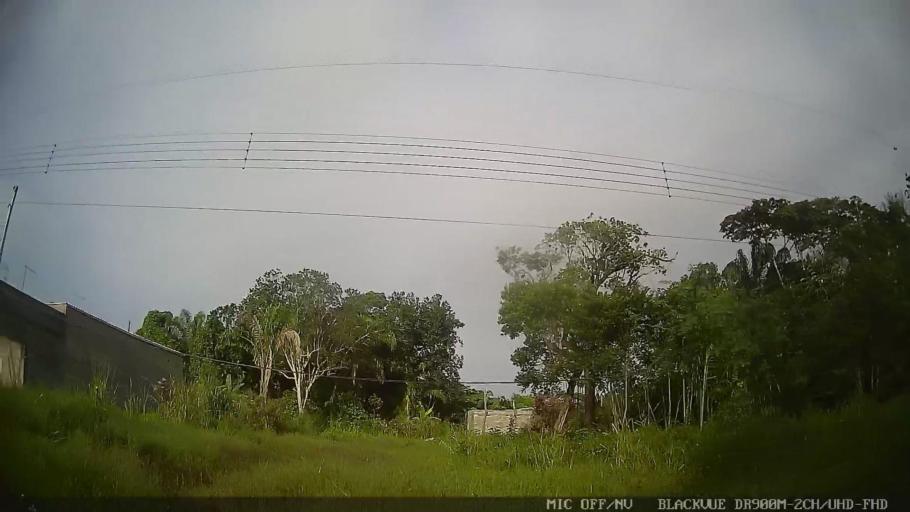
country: BR
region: Sao Paulo
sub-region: Peruibe
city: Peruibe
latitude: -24.2370
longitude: -46.9141
